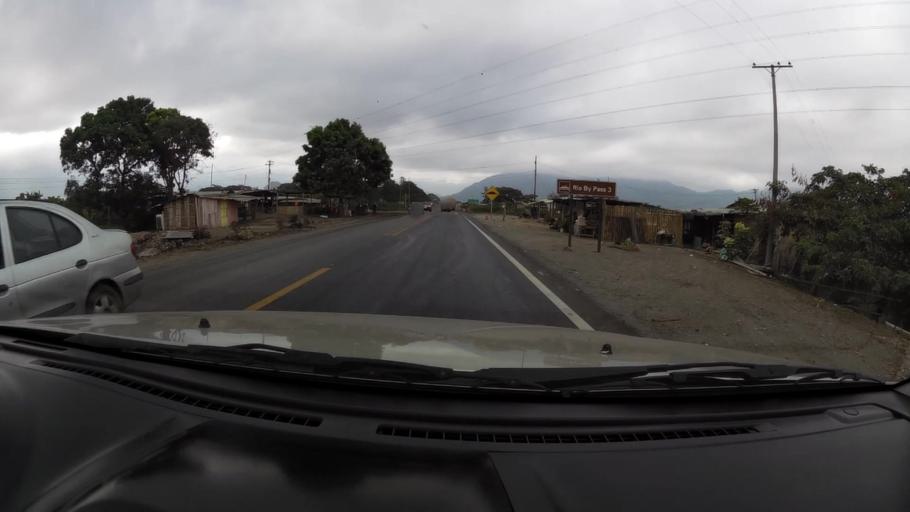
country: EC
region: Guayas
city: Coronel Marcelino Mariduena
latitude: -2.3484
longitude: -79.6343
